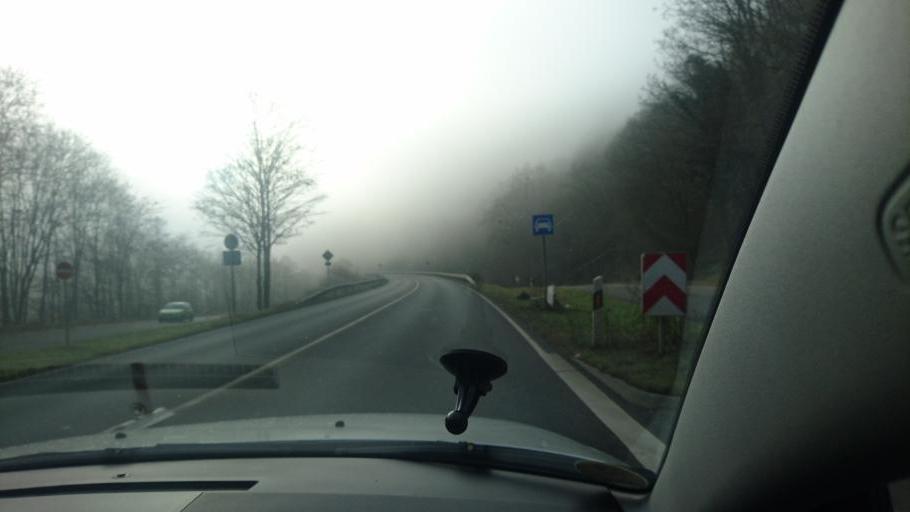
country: DE
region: Rheinland-Pfalz
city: Lahnstein
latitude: 50.3155
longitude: 7.6240
